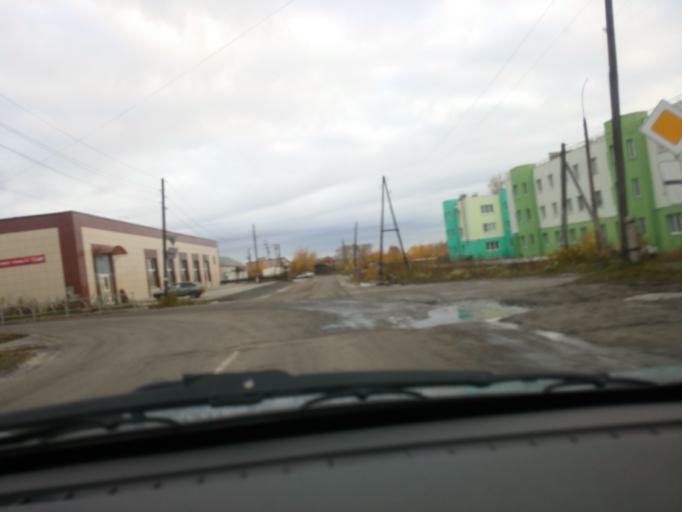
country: RU
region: Sverdlovsk
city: Turinsk
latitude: 58.0407
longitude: 63.7071
